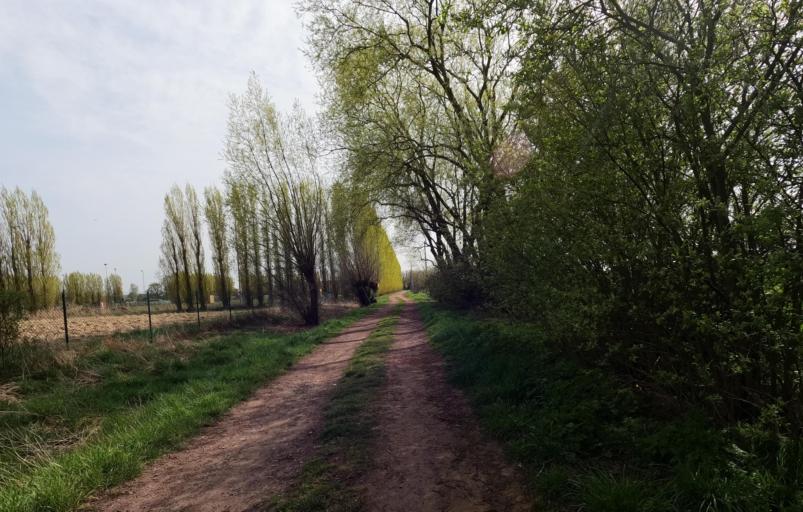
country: BE
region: Flanders
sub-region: Provincie Antwerpen
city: Kapellen
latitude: 51.2979
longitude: 4.4075
